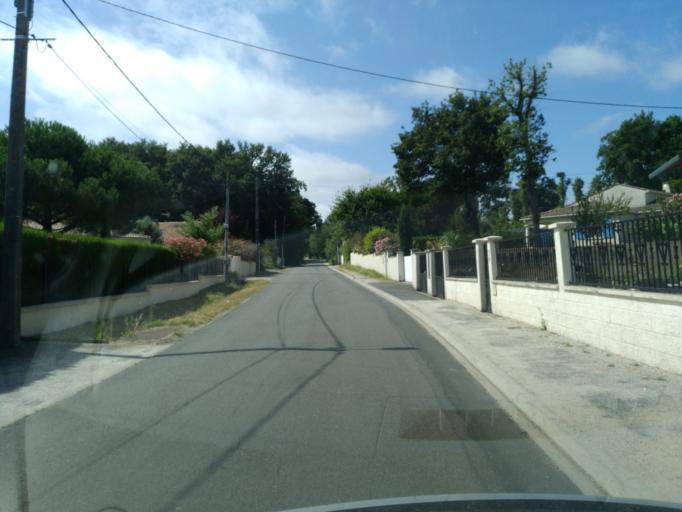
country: FR
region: Poitou-Charentes
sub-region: Departement de la Charente-Maritime
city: Breuillet
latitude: 45.6939
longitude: -1.0693
